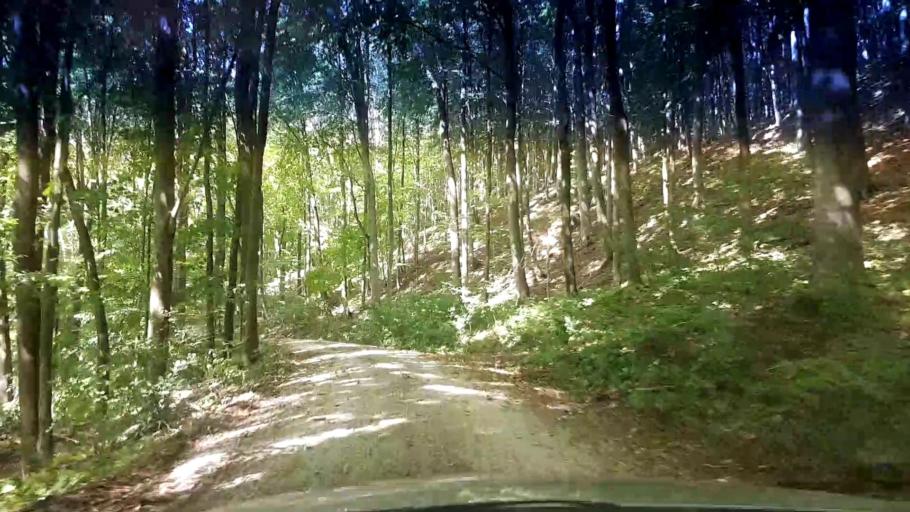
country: DE
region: Bavaria
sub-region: Upper Franconia
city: Schesslitz
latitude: 49.9457
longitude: 11.0685
